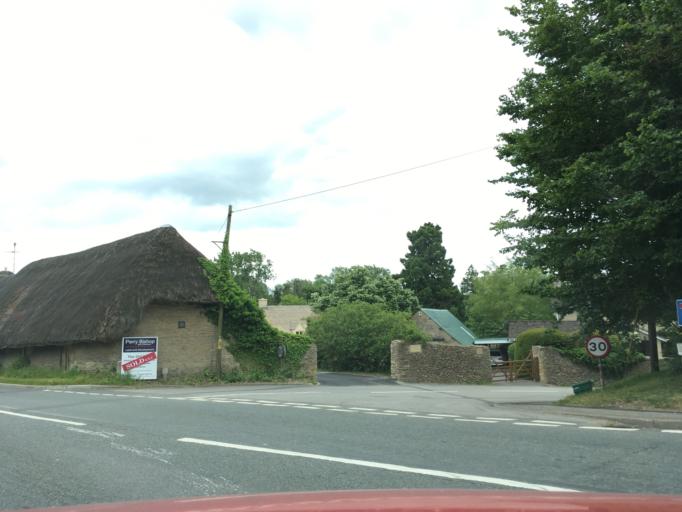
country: GB
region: England
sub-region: Gloucestershire
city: Cirencester
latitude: 51.7334
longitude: -1.9838
